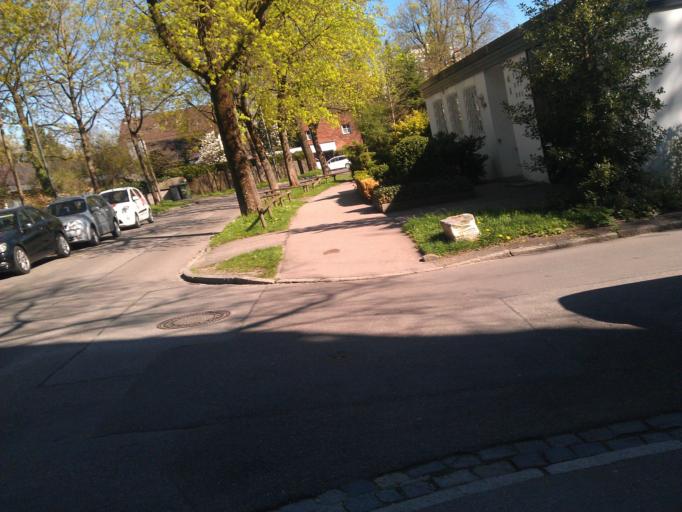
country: DE
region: Bavaria
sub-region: Swabia
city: Augsburg
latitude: 48.3594
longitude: 10.9158
